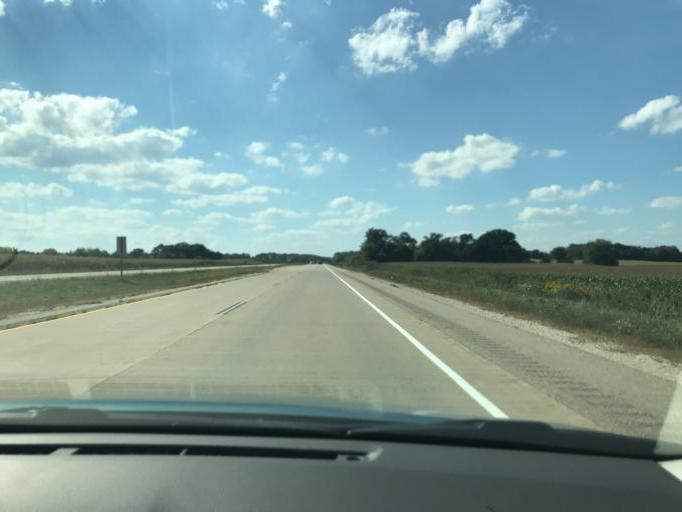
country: US
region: Wisconsin
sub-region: Kenosha County
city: Twin Lakes
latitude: 42.5813
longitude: -88.2424
